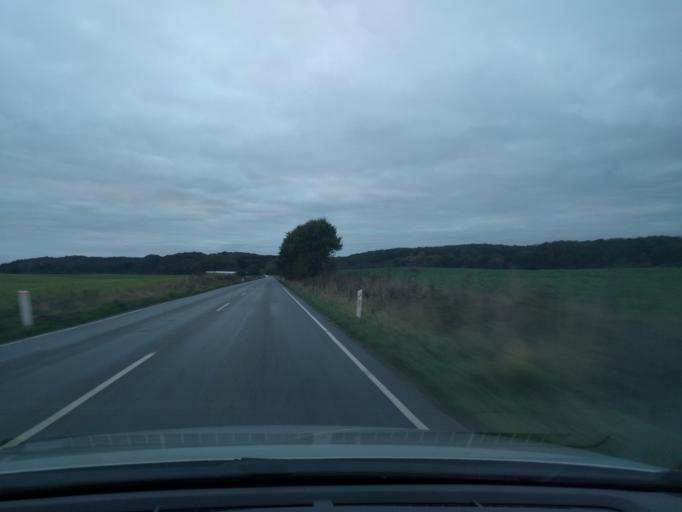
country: DK
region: South Denmark
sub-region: Odense Kommune
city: Bellinge
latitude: 55.2183
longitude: 10.3059
